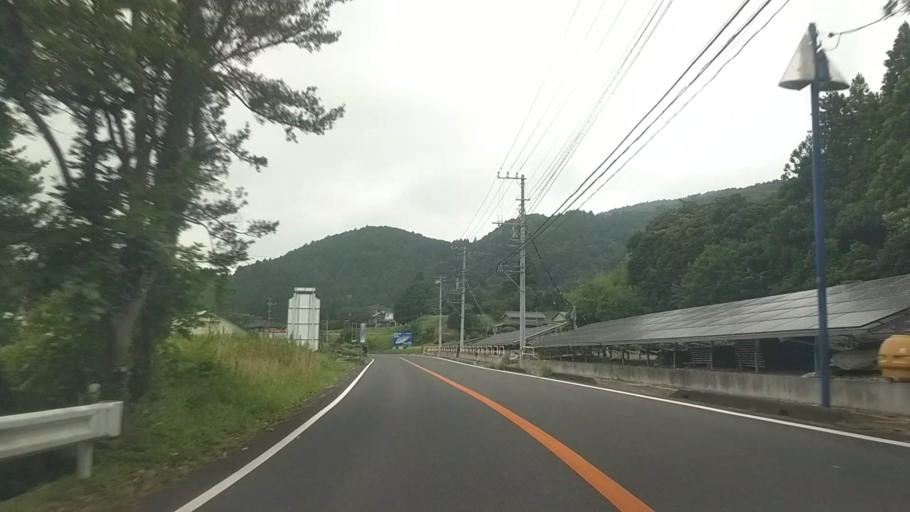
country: JP
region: Chiba
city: Kawaguchi
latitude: 35.1421
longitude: 139.9727
